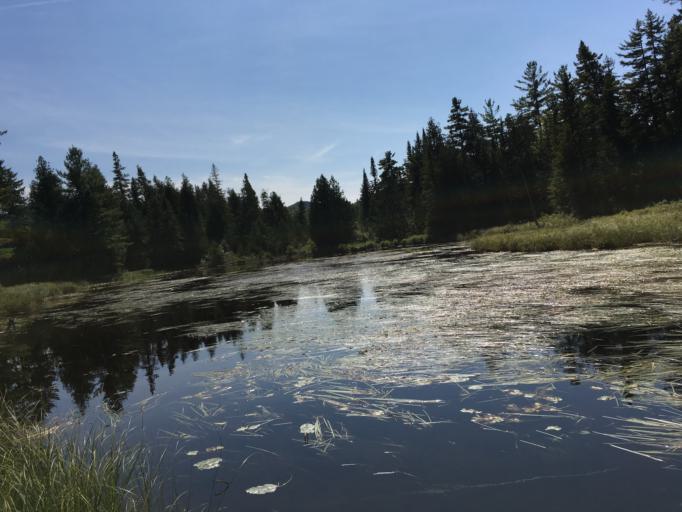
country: US
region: Maine
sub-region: Penobscot County
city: Millinocket
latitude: 45.8625
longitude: -68.6748
